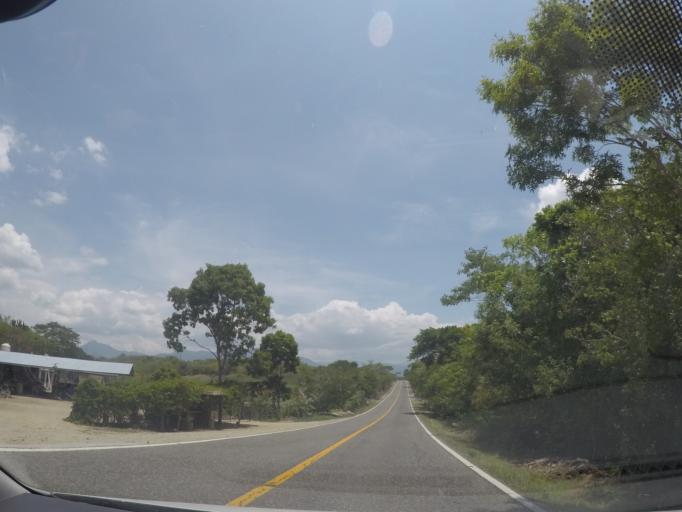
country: MX
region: Oaxaca
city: Asuncion Tlacolulita
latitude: 16.3999
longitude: -95.7796
